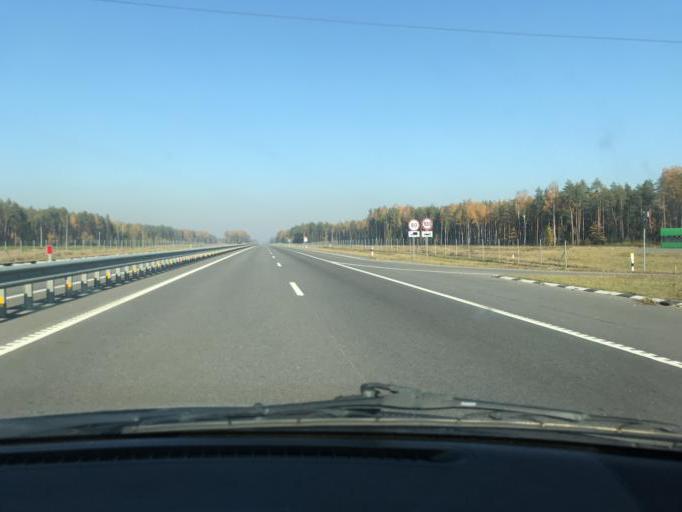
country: BY
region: Minsk
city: Slutsk
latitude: 53.2312
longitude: 27.5505
